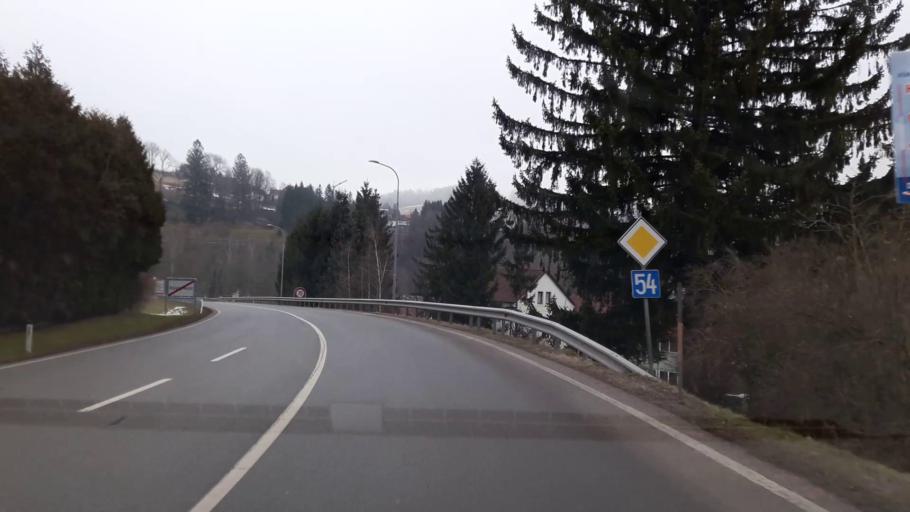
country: AT
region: Lower Austria
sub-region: Politischer Bezirk Neunkirchen
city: Thomasberg
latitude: 47.5522
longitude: 16.0871
